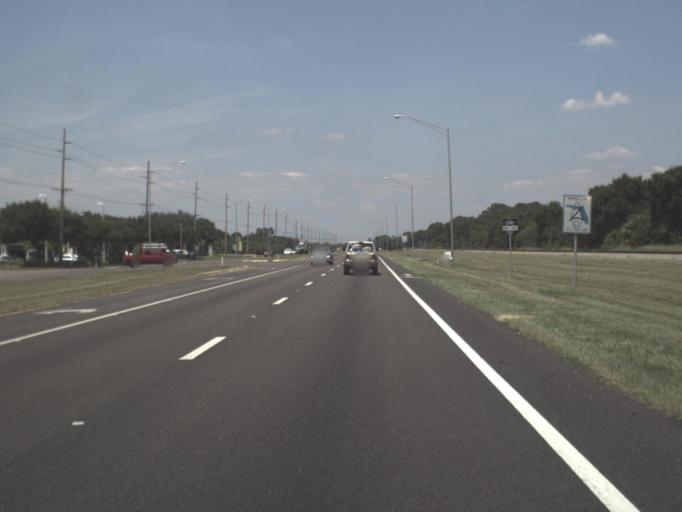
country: US
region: Florida
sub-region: Hillsborough County
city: Apollo Beach
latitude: 27.7700
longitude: -82.3911
